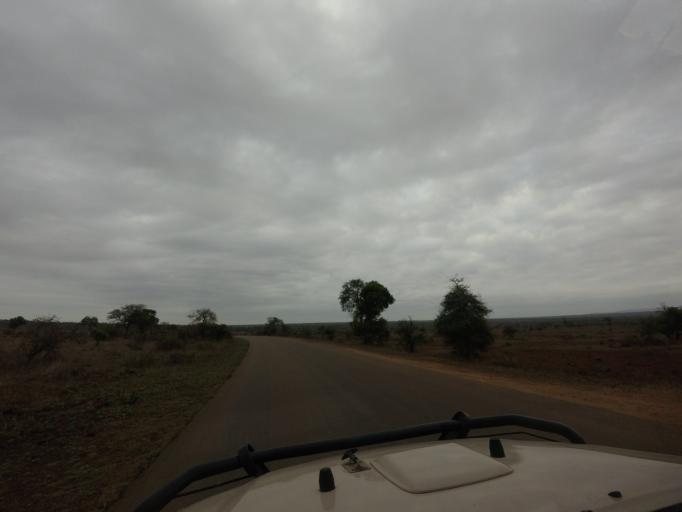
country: ZA
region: Mpumalanga
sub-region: Ehlanzeni District
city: Komatipoort
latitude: -25.3453
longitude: 31.8837
